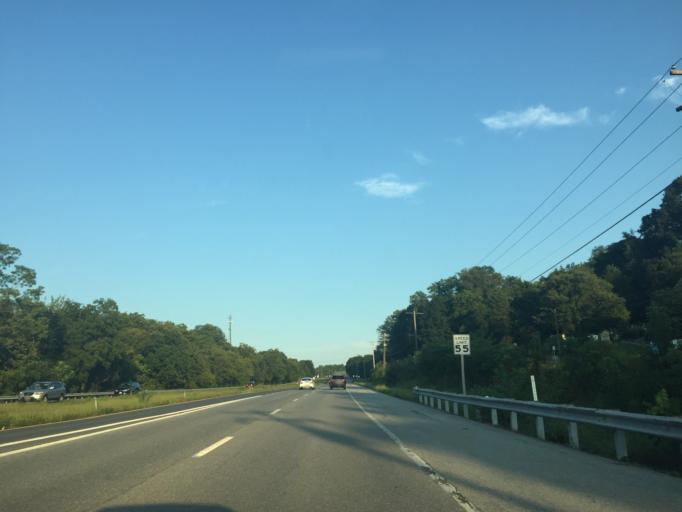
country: US
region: Maryland
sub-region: Frederick County
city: Spring Ridge
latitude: 39.3954
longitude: -77.3389
